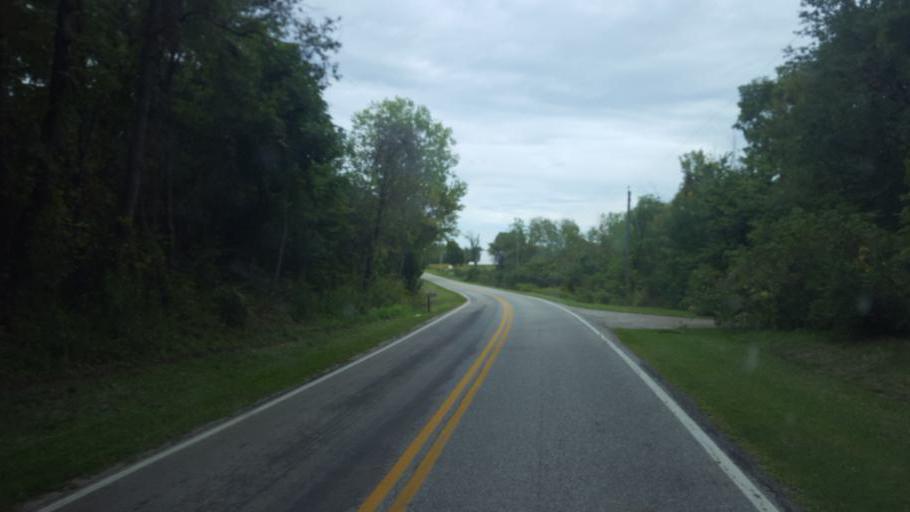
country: US
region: Ohio
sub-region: Delaware County
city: Sunbury
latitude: 40.2555
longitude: -82.8235
